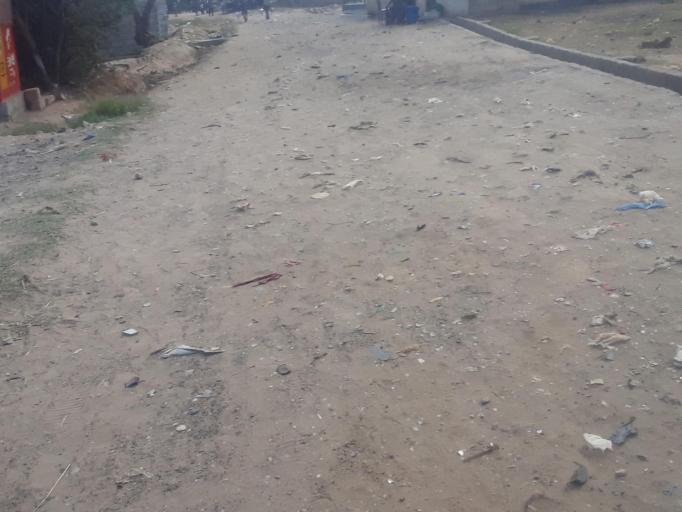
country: ZM
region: Lusaka
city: Lusaka
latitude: -15.3593
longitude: 28.3076
